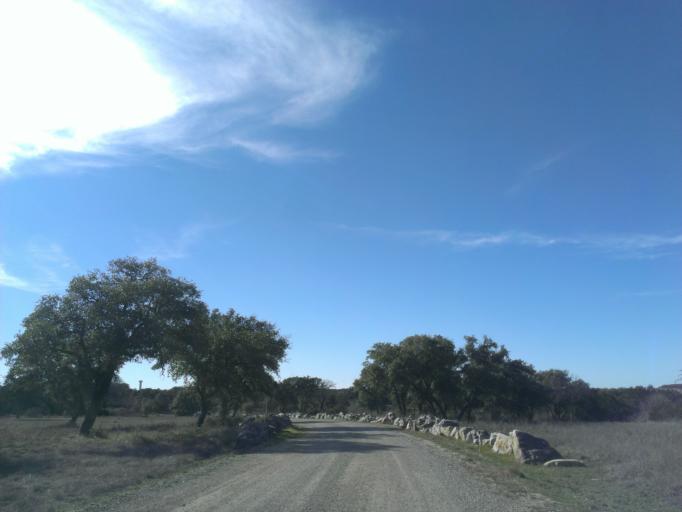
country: US
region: Texas
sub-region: Burnet County
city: Meadowlakes
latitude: 30.5288
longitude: -98.2659
